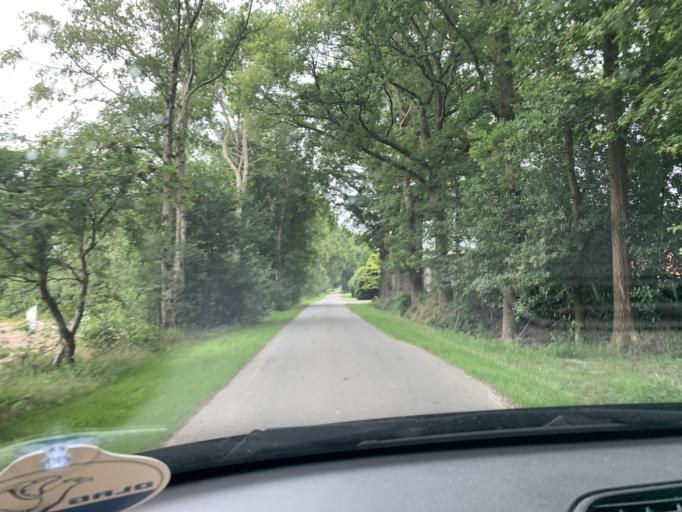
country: DE
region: Lower Saxony
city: Apen
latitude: 53.1815
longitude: 7.7838
